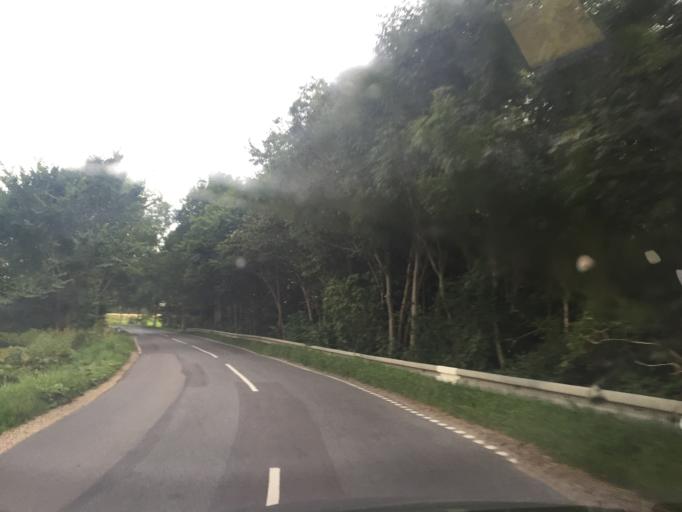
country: DK
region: Capital Region
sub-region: Egedal Kommune
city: Vekso
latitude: 55.6975
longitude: 12.2326
